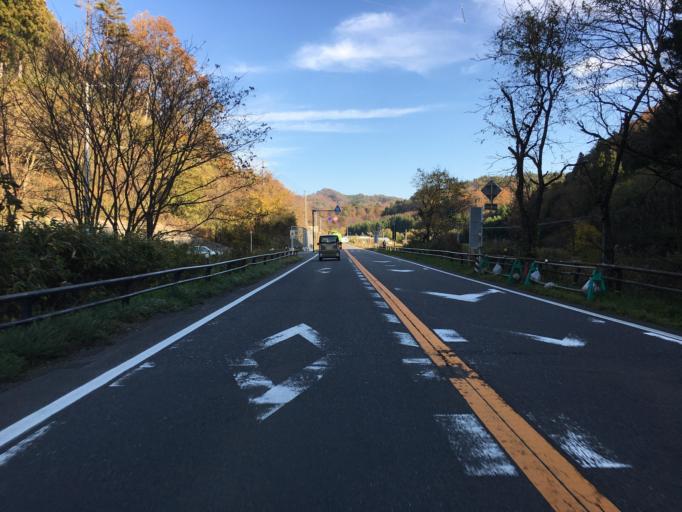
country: JP
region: Fukushima
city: Sukagawa
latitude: 37.3014
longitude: 140.4993
